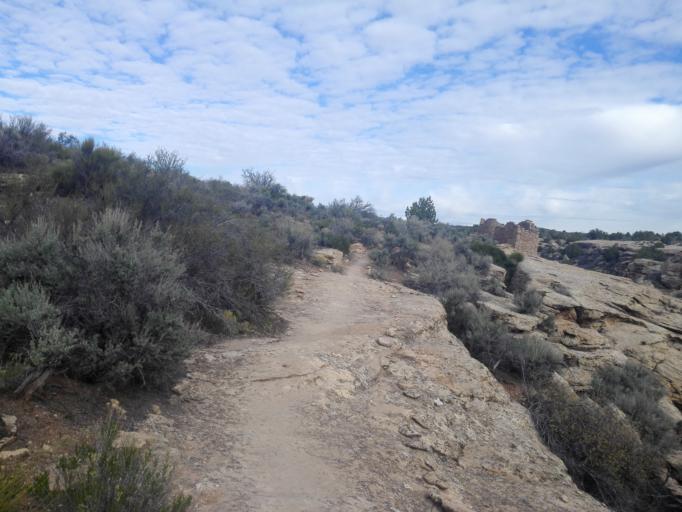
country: US
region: Colorado
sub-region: Montezuma County
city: Towaoc
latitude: 37.3827
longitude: -109.0767
